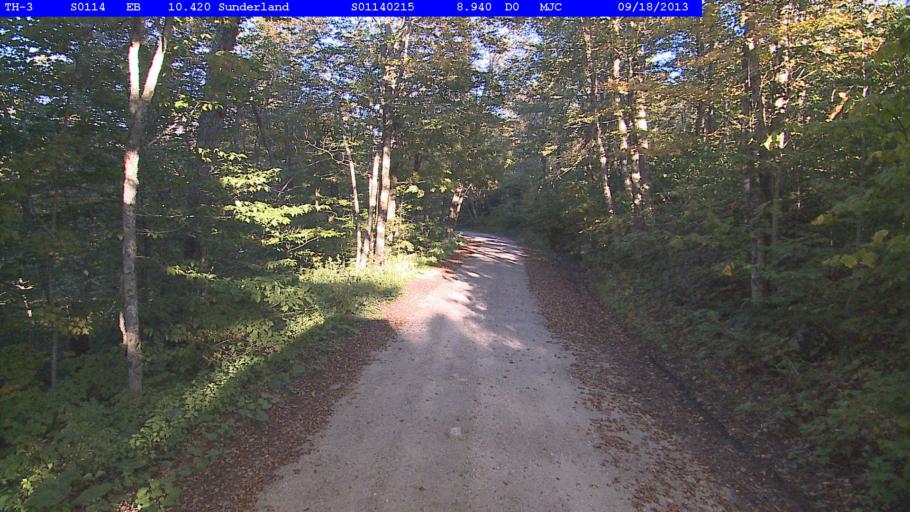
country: US
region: Vermont
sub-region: Bennington County
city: Manchester Center
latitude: 43.0557
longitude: -73.0154
